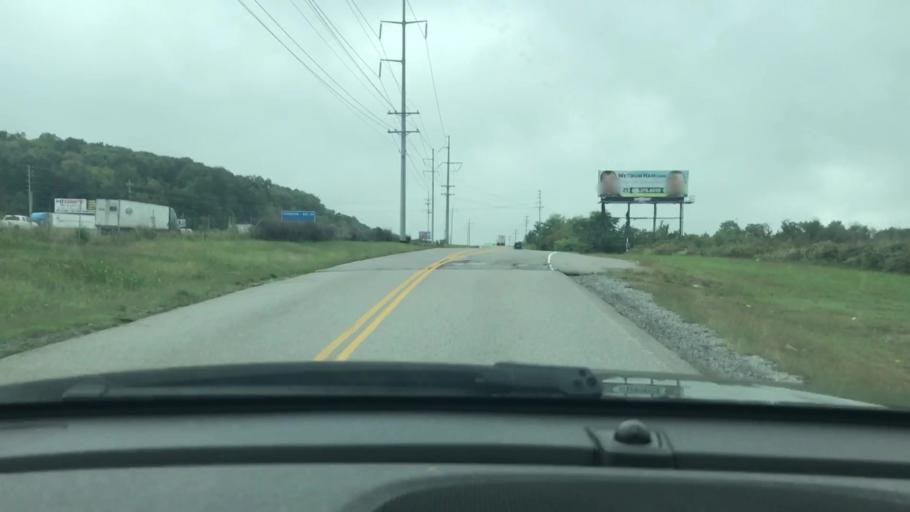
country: US
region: Tennessee
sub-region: Rutherford County
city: La Vergne
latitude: 35.9797
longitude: -86.5747
